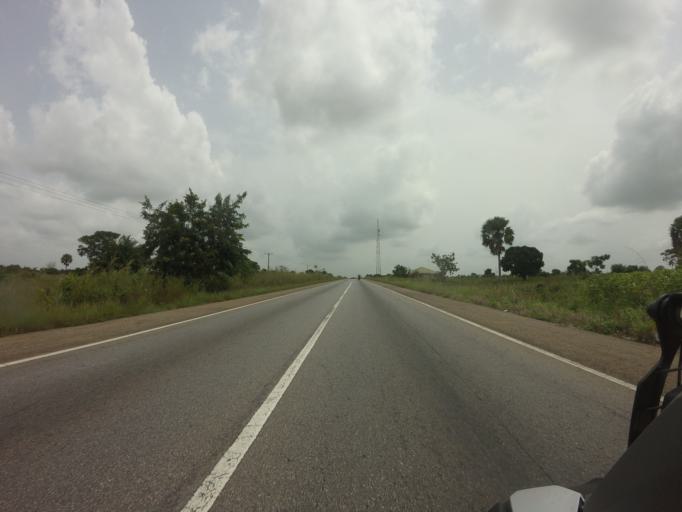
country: GH
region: Volta
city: Keta
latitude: 6.0470
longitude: 0.7216
